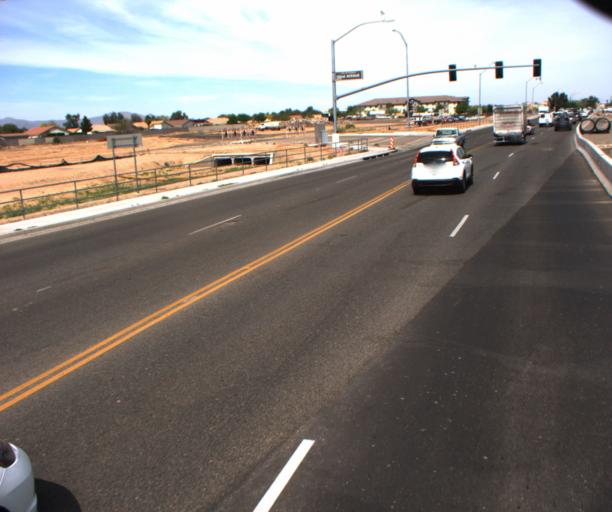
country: US
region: Arizona
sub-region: Maricopa County
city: Surprise
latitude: 33.6338
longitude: -112.3438
